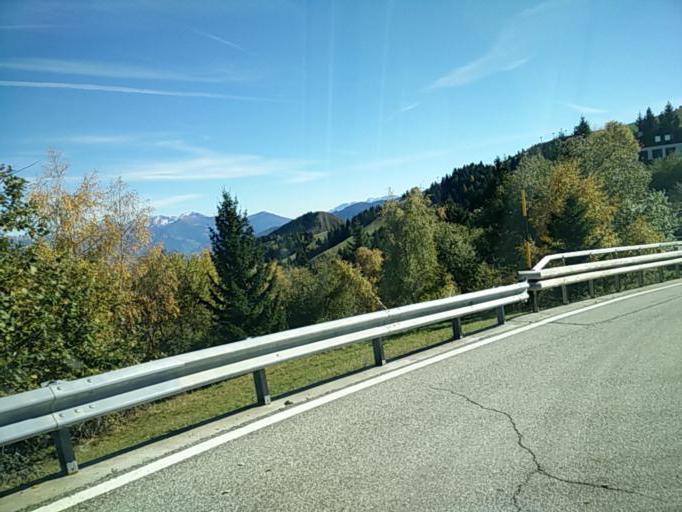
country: IT
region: Trentino-Alto Adige
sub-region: Provincia di Trento
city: Cadine
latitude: 46.0448
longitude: 11.0609
